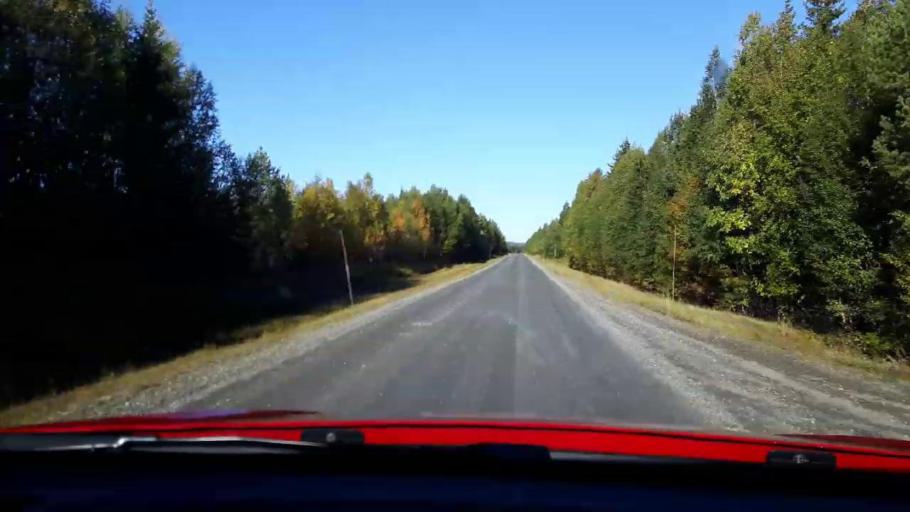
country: NO
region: Nord-Trondelag
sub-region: Lierne
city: Sandvika
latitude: 64.5255
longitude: 14.0627
